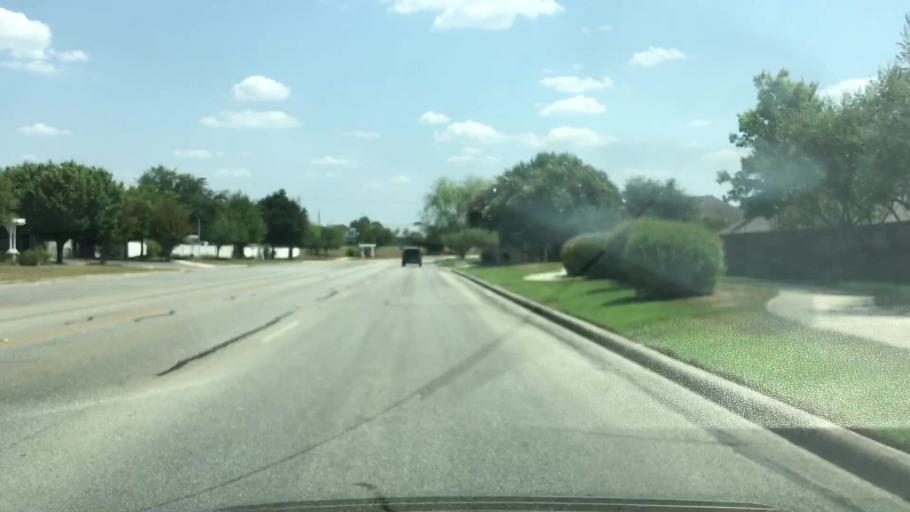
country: US
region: Texas
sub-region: Guadalupe County
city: Cibolo
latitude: 29.5918
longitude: -98.2500
